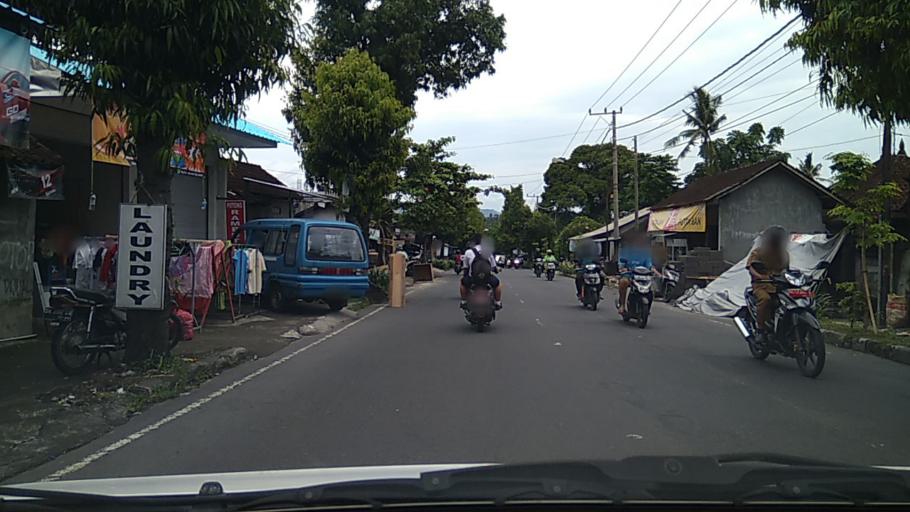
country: ID
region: Bali
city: Banjar Kelodan
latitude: -8.5394
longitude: 115.3415
